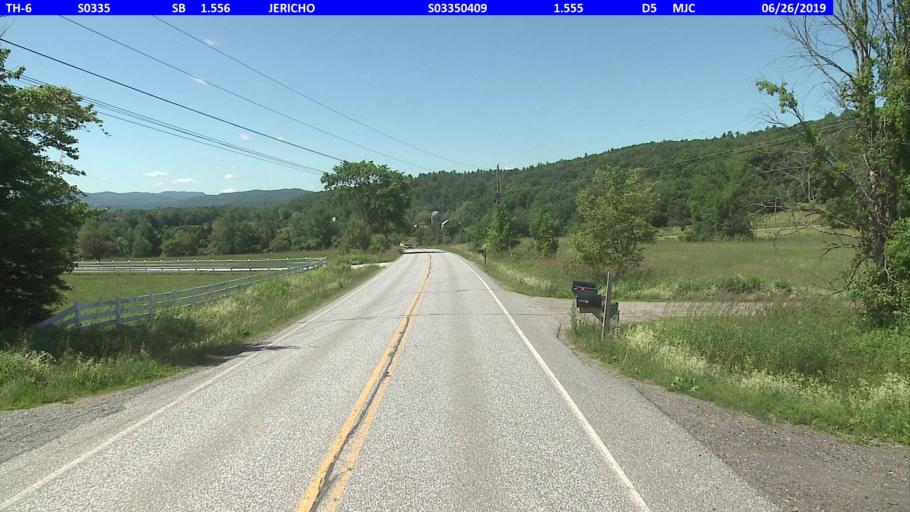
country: US
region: Vermont
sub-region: Chittenden County
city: Jericho
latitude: 44.4861
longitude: -73.0136
